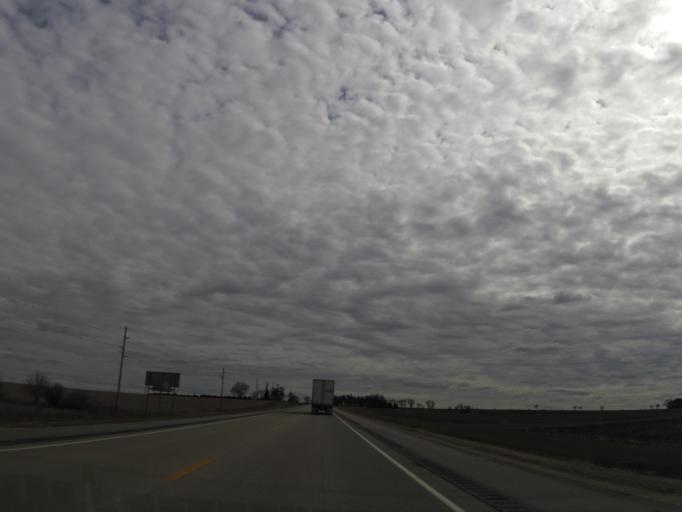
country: US
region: Minnesota
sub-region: Fillmore County
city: Spring Valley
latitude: 43.5993
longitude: -92.3894
